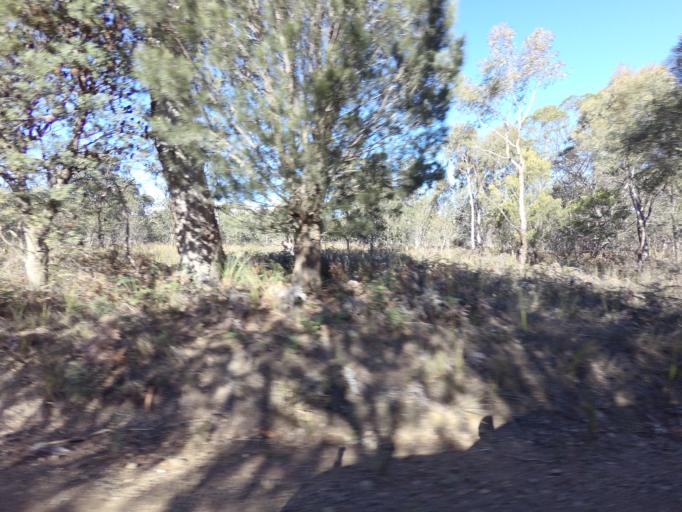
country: AU
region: Tasmania
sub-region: Sorell
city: Sorell
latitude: -42.3510
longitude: 147.9710
